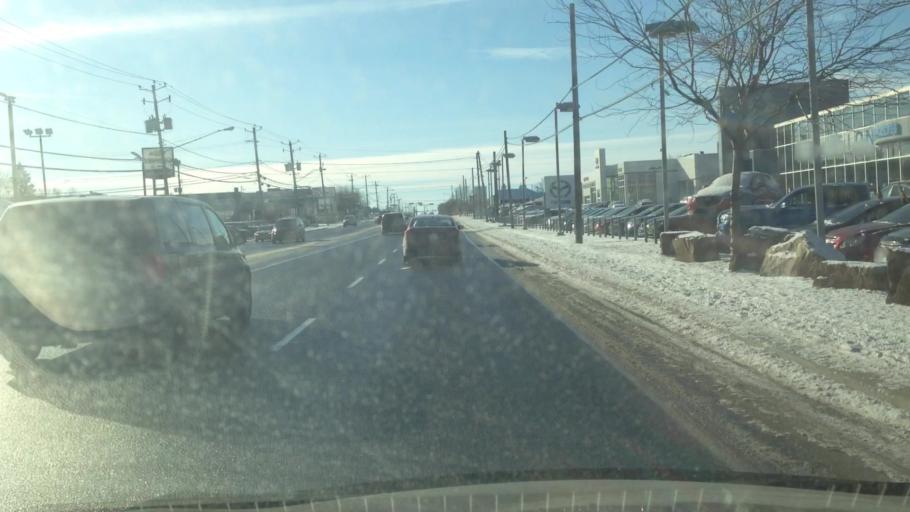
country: CA
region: Quebec
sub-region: Monteregie
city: Chateauguay
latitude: 45.3523
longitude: -73.7199
